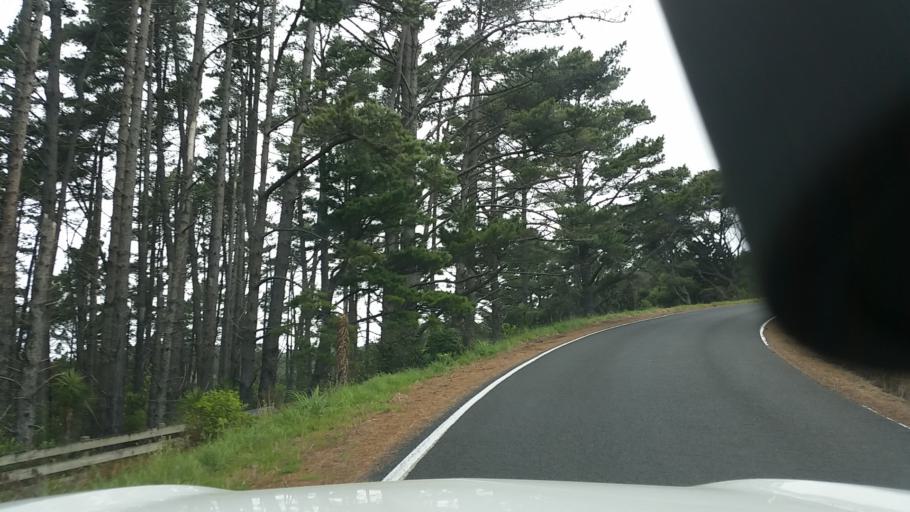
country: NZ
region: Auckland
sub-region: Auckland
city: Muriwai Beach
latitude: -36.8736
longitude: 174.4640
